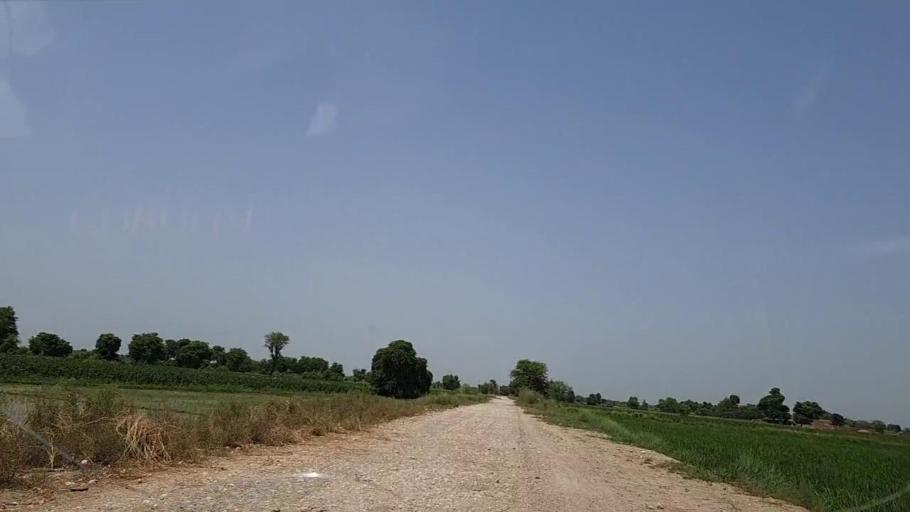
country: PK
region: Sindh
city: Tharu Shah
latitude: 26.9509
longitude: 68.0436
